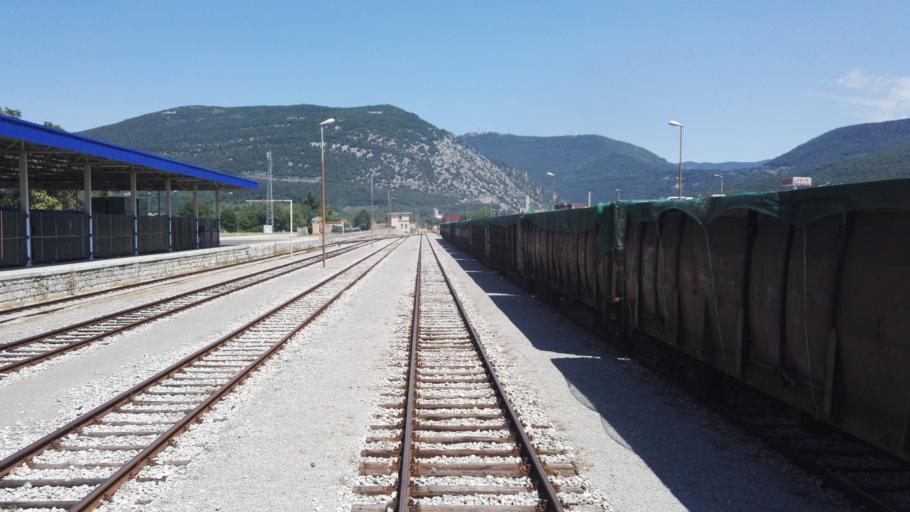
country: SI
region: Nova Gorica
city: Nova Gorica
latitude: 45.9590
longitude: 13.6370
